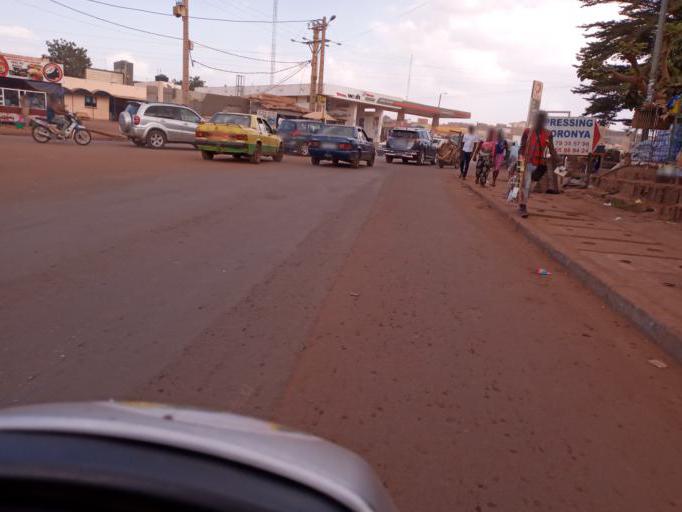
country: ML
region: Bamako
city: Bamako
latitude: 12.5975
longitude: -7.9385
